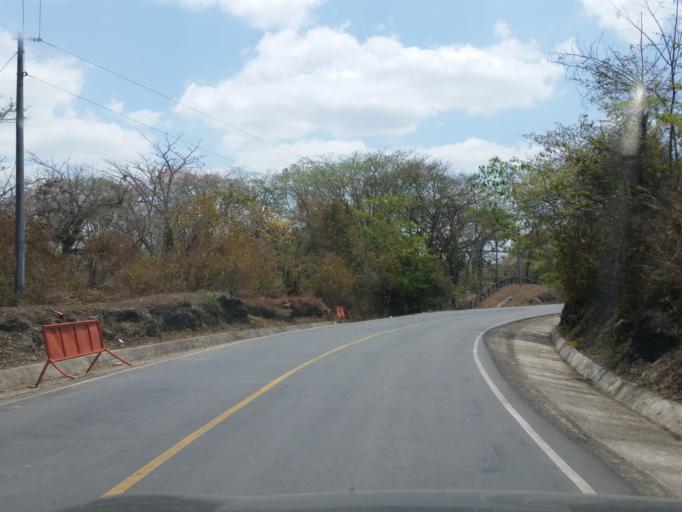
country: NI
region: Matagalpa
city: Muy Muy
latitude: 12.6852
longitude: -85.5396
